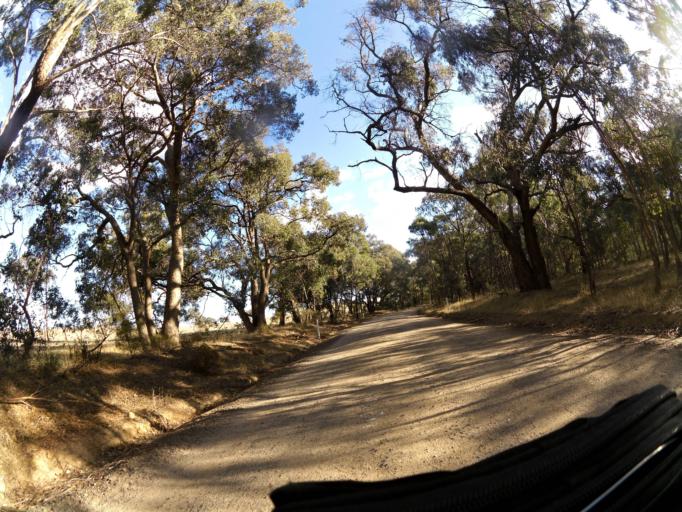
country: AU
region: Victoria
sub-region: Greater Bendigo
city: Kennington
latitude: -37.0196
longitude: 144.8048
